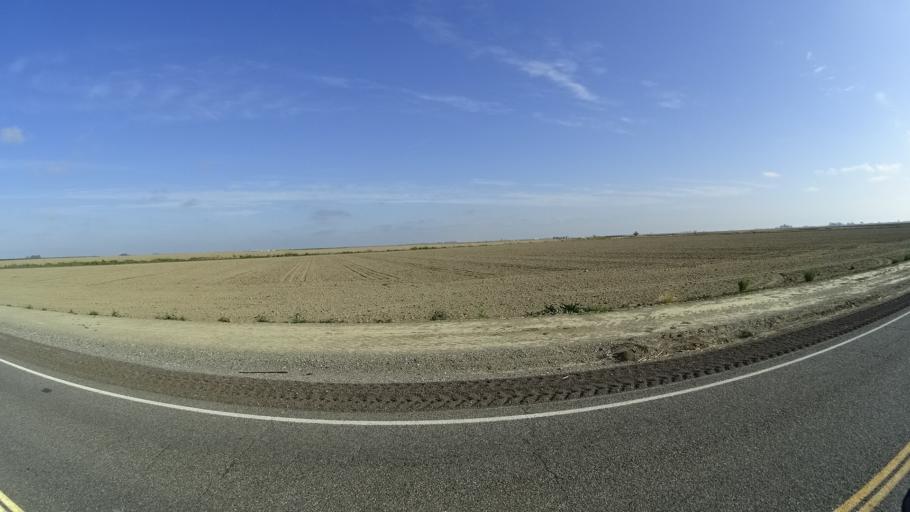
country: US
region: California
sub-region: Glenn County
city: Willows
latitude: 39.5821
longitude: -122.1197
